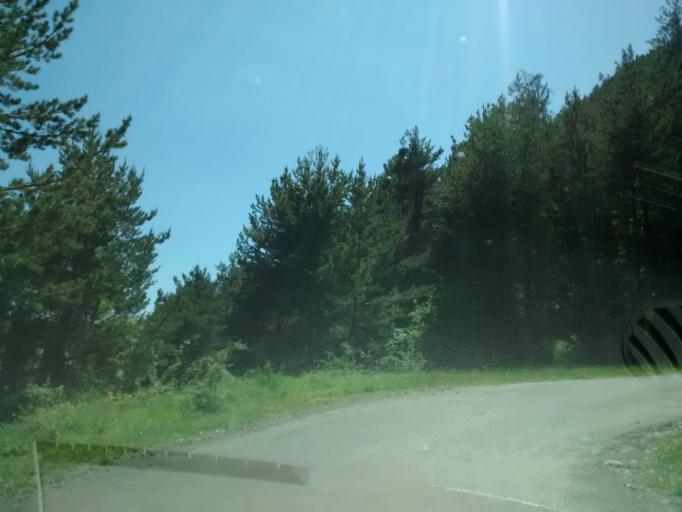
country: ES
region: Aragon
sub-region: Provincia de Huesca
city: Borau
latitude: 42.7218
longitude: -0.6020
